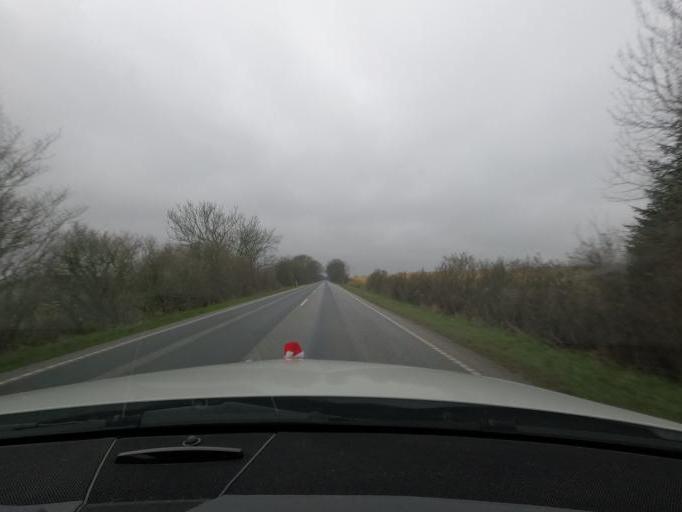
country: DK
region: South Denmark
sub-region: Haderslev Kommune
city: Starup
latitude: 55.2126
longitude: 9.5898
